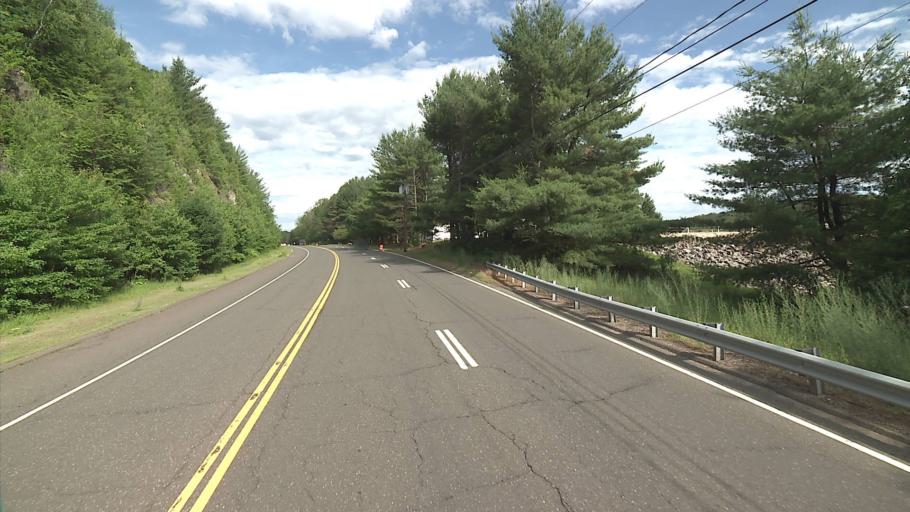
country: US
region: Connecticut
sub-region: New Haven County
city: Naugatuck
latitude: 41.5134
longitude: -73.0668
